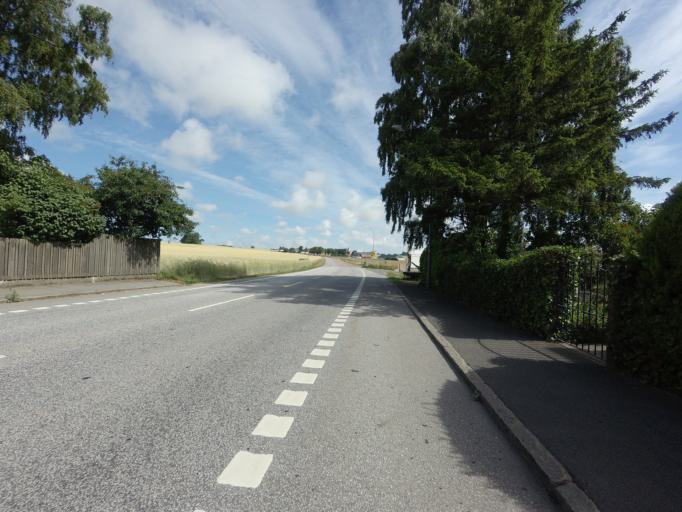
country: SE
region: Skane
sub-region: Simrishamns Kommun
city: Simrishamn
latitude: 55.4784
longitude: 14.2838
